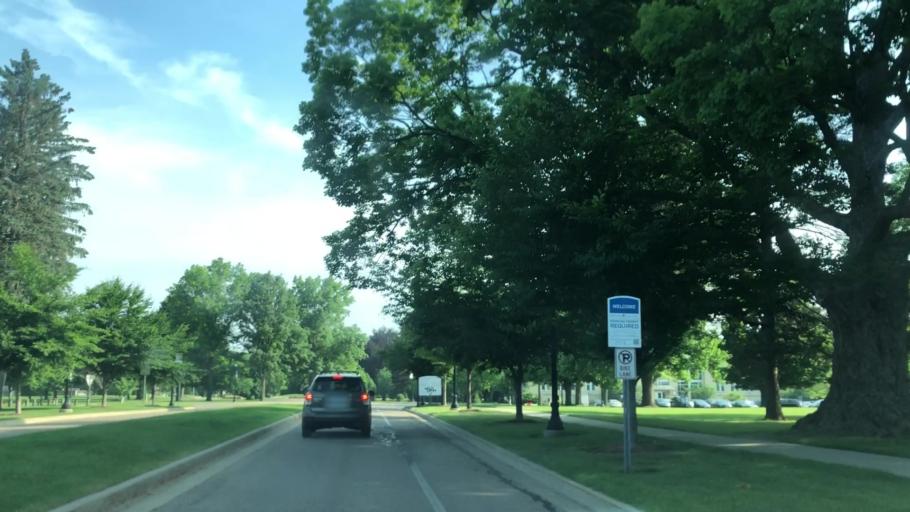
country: US
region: Michigan
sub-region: Berrien County
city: Berrien Springs
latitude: 41.9601
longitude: -86.3587
